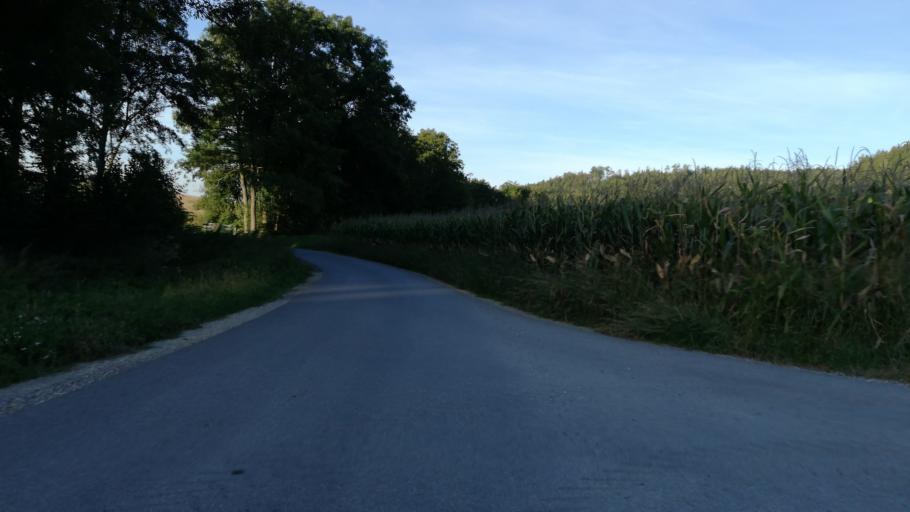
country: AT
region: Upper Austria
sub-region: Wels-Land
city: Edt bei Lambach
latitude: 48.1726
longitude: 13.8928
